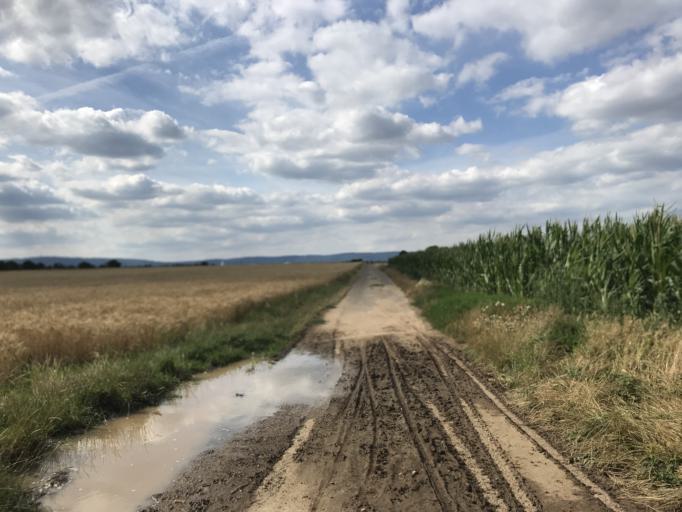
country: DE
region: Hesse
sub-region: Regierungsbezirk Darmstadt
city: Hochheim am Main
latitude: 50.0333
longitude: 8.3092
